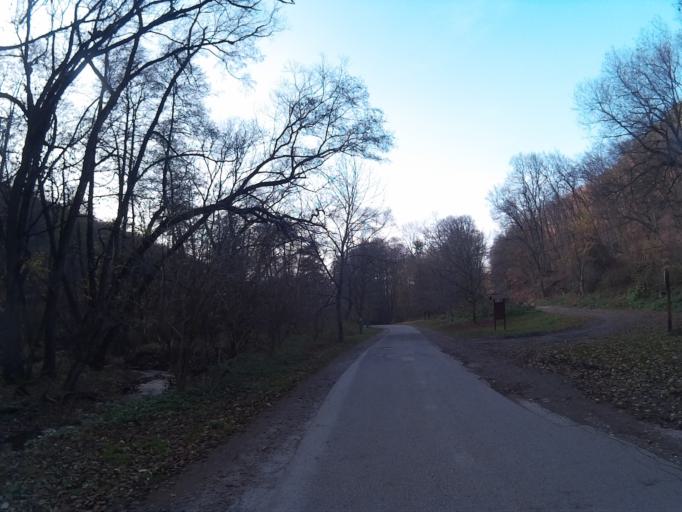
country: HU
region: Heves
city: Szilvasvarad
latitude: 48.0921
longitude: 20.3978
